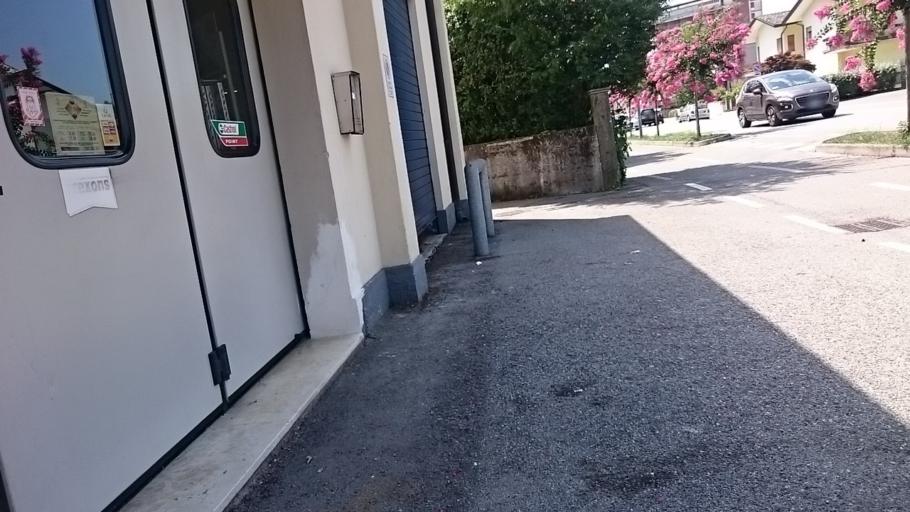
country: IT
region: Veneto
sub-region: Provincia di Padova
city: Cittadella
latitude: 45.6468
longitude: 11.7722
